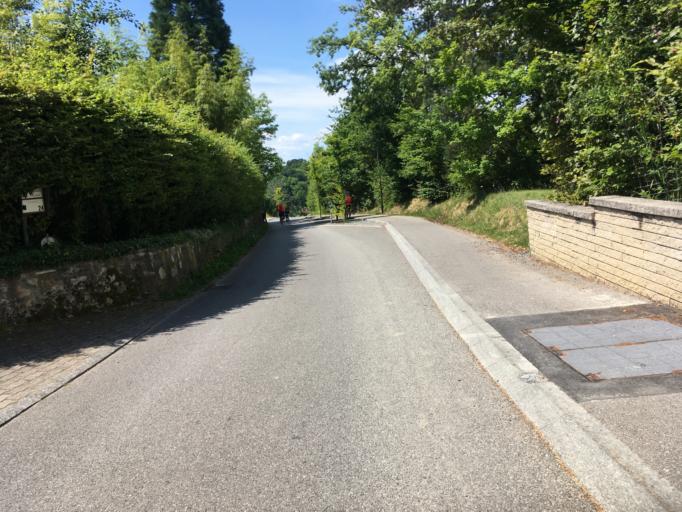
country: CH
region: Fribourg
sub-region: Broye District
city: Domdidier
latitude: 46.9201
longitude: 6.9607
